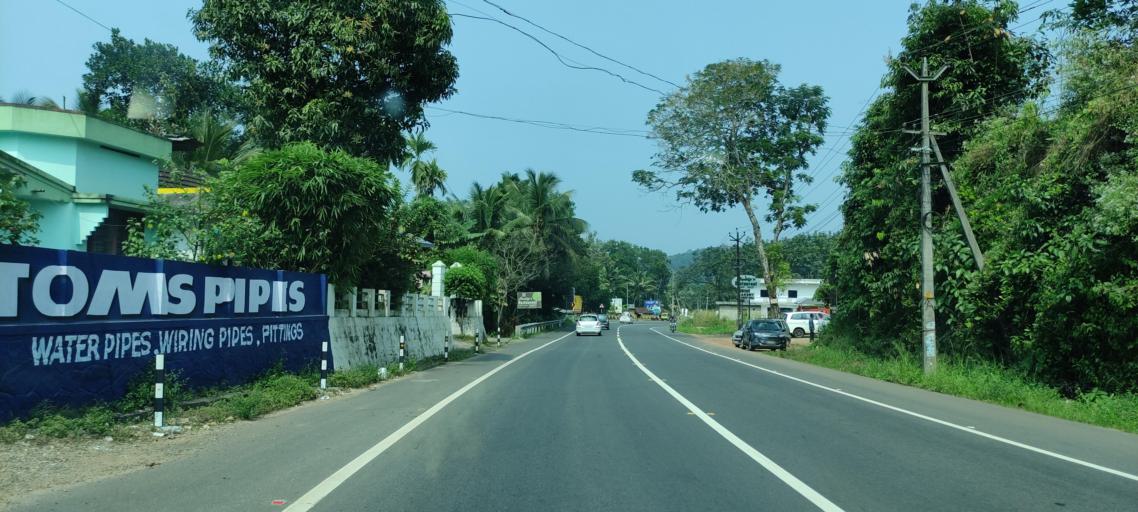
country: IN
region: Kerala
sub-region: Pattanamtitta
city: Adur
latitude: 9.1799
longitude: 76.7088
